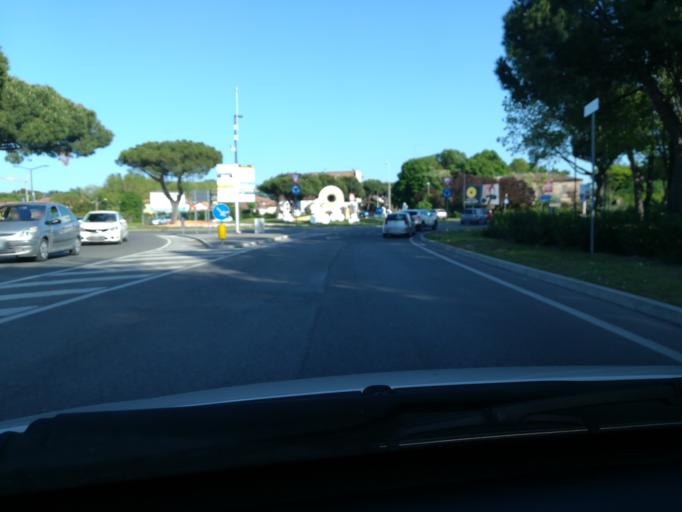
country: IT
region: Emilia-Romagna
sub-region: Provincia di Rimini
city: Riccione
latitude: 43.9989
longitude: 12.6462
